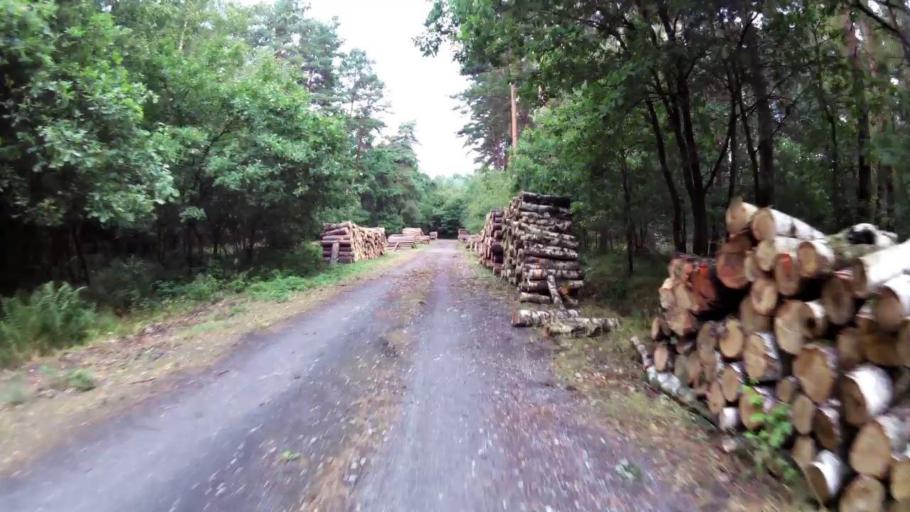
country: PL
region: West Pomeranian Voivodeship
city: Trzcinsko Zdroj
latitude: 52.8875
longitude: 14.6788
